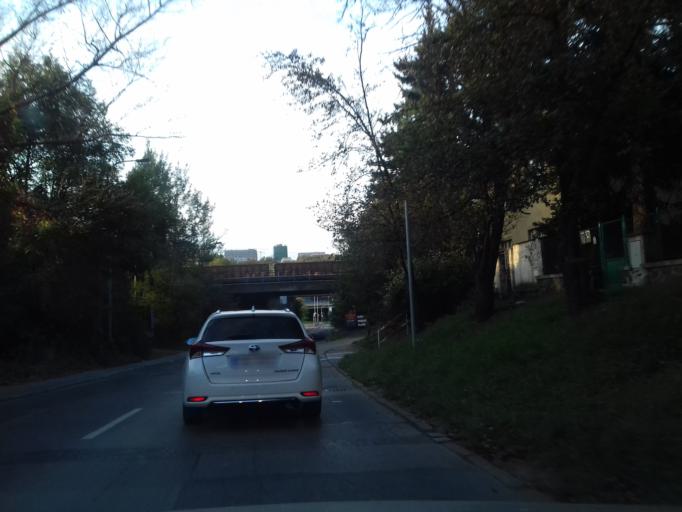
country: CZ
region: Praha
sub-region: Praha 4
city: Hodkovicky
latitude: 50.0326
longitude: 14.4443
